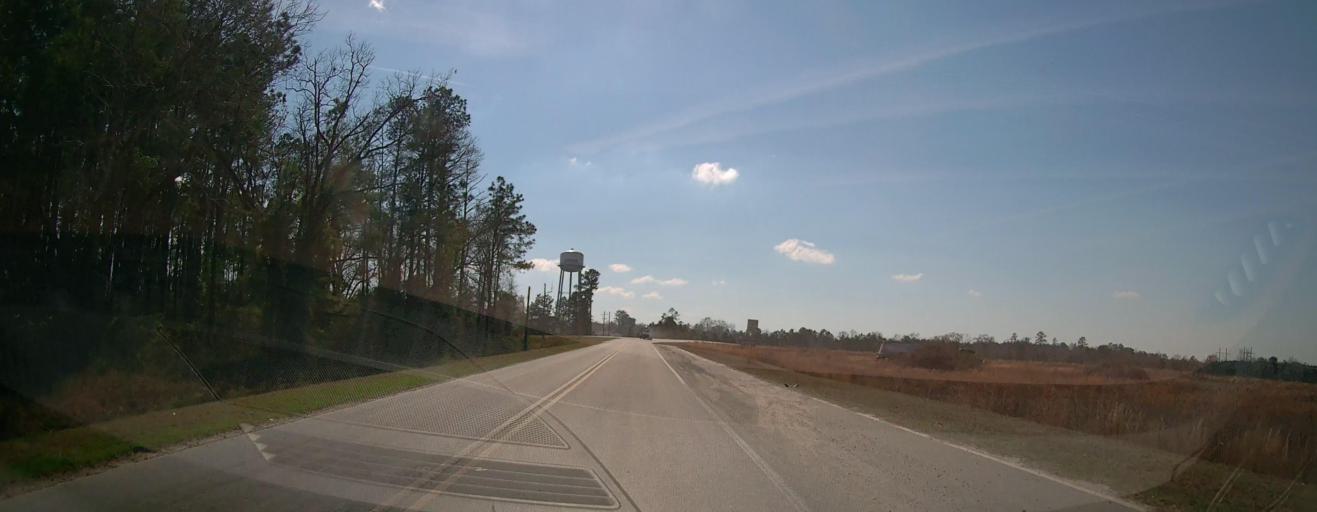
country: US
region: Georgia
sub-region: Wilkinson County
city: Gordon
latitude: 32.8954
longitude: -83.3066
